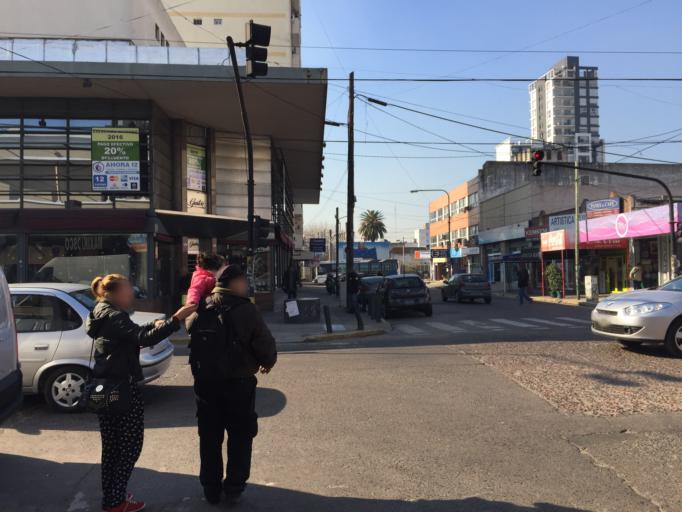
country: AR
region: Buenos Aires
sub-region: Partido de Lomas de Zamora
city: Lomas de Zamora
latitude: -34.7621
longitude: -58.3986
